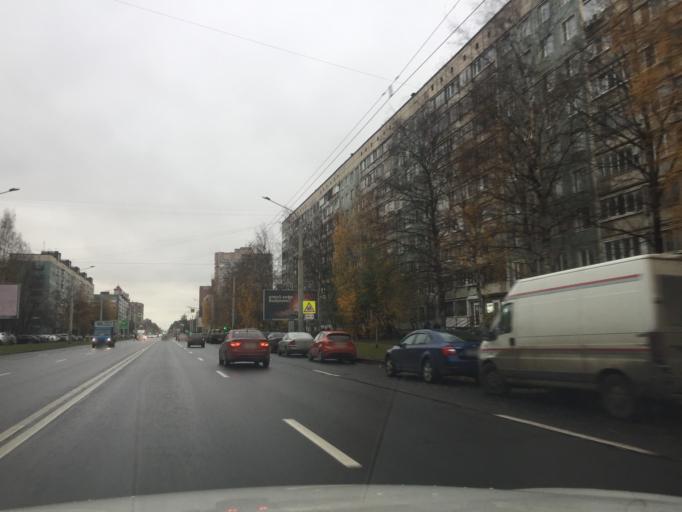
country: RU
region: Leningrad
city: Akademicheskoe
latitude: 60.0244
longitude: 30.3811
